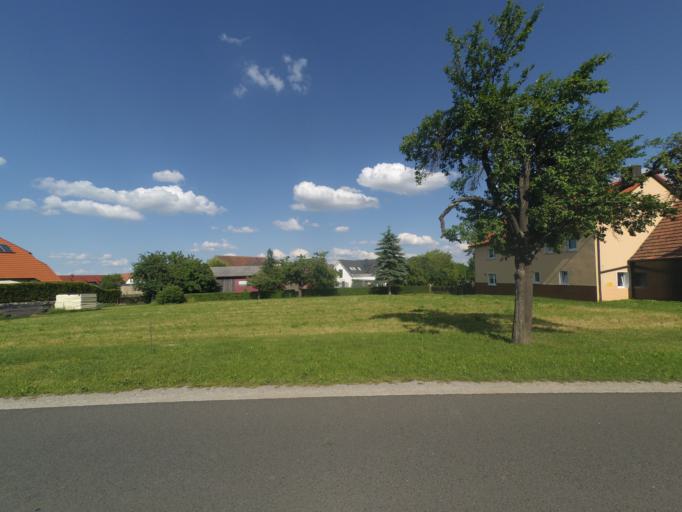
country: DE
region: Bavaria
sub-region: Regierungsbezirk Mittelfranken
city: Wilhermsdorf
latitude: 49.5165
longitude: 10.7202
